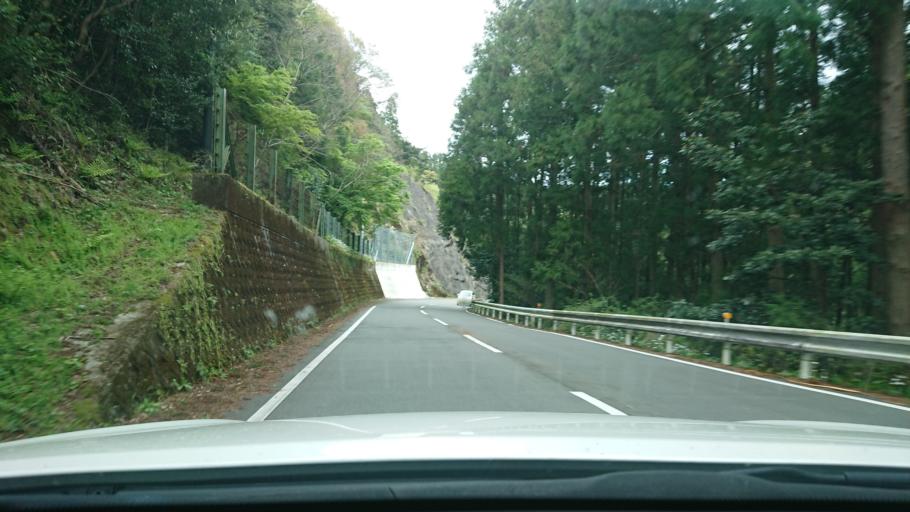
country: JP
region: Tokushima
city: Ishii
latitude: 33.9103
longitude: 134.4212
